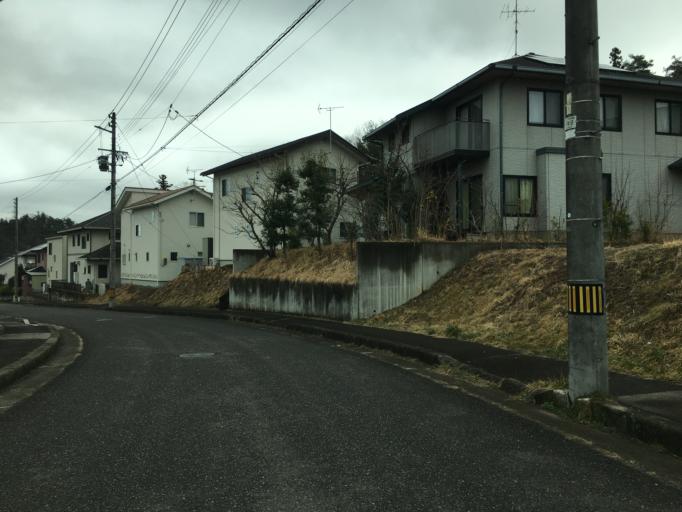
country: JP
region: Fukushima
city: Fukushima-shi
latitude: 37.7164
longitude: 140.4071
